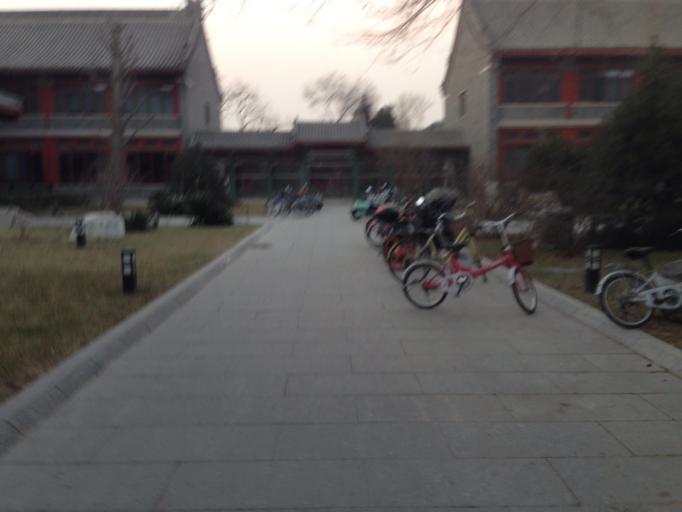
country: CN
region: Beijing
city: Haidian
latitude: 39.9960
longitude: 116.3054
